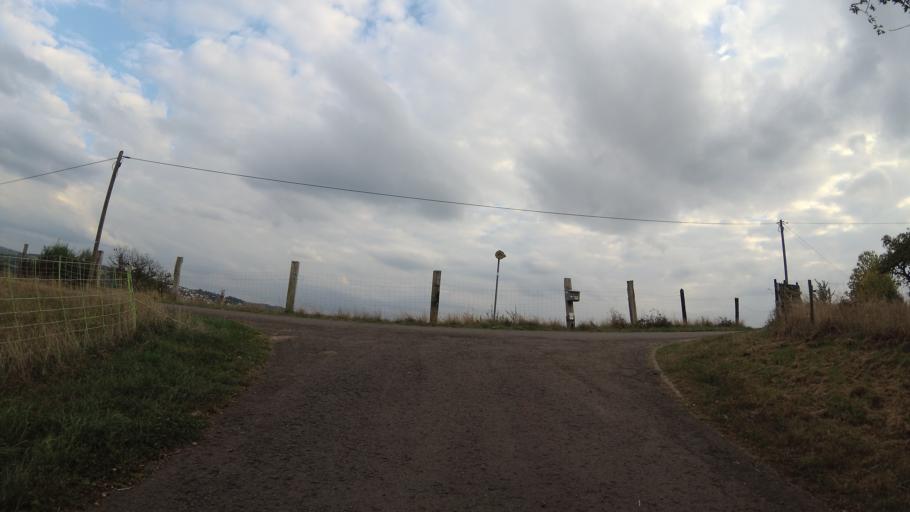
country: DE
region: Saarland
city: Ottweiler
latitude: 49.4147
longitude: 7.1522
